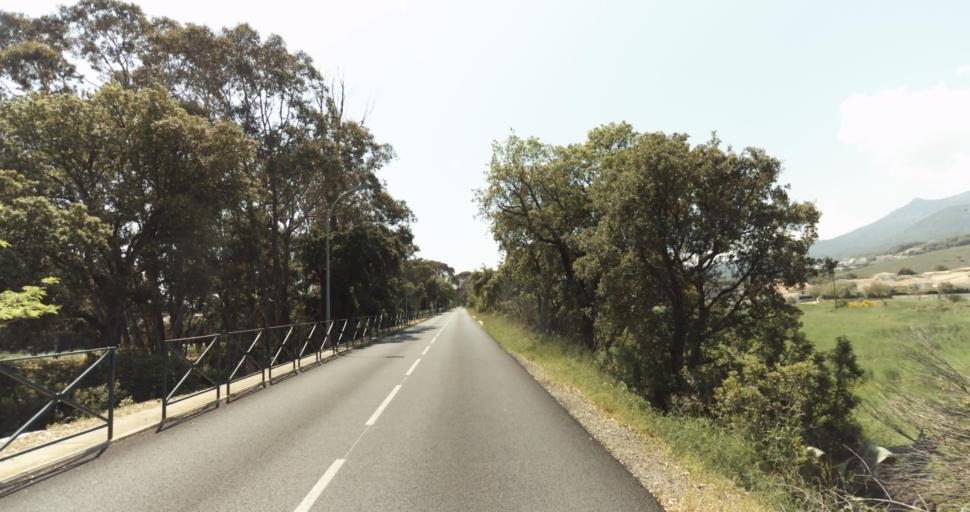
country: FR
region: Corsica
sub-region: Departement de la Haute-Corse
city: Biguglia
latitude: 42.6026
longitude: 9.4345
